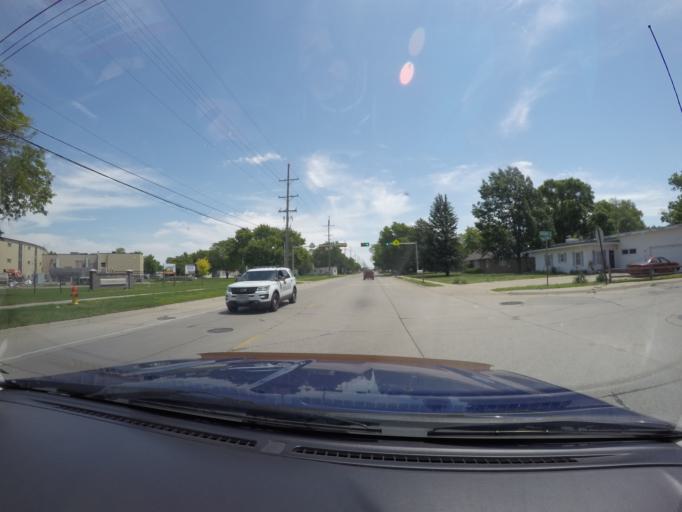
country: US
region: Nebraska
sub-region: Hall County
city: Grand Island
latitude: 40.9022
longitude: -98.3447
